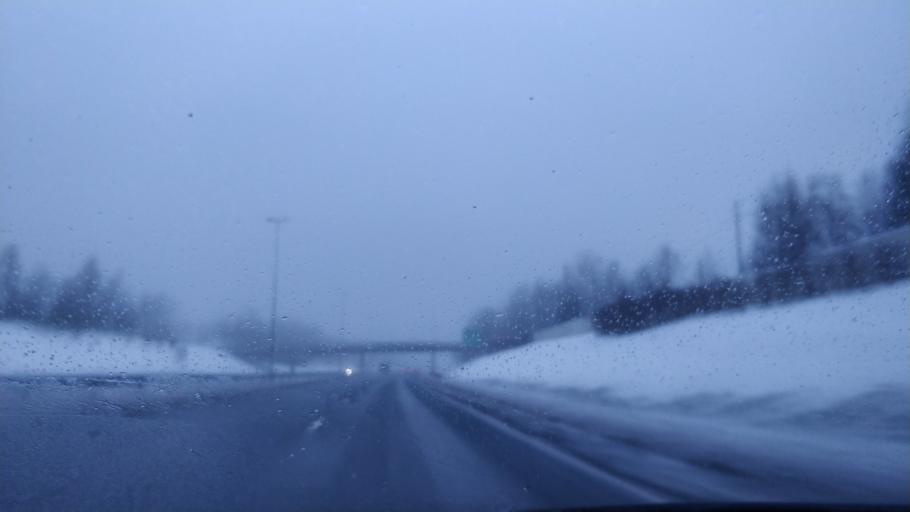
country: FI
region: Lapland
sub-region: Kemi-Tornio
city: Kemi
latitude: 65.7492
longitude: 24.5769
